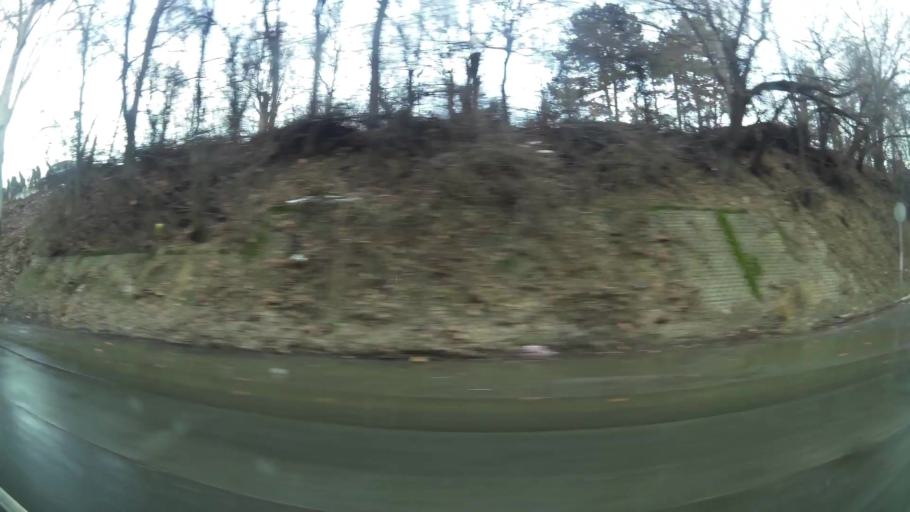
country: RS
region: Central Serbia
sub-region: Belgrade
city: Vozdovac
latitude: 44.7525
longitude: 20.4821
